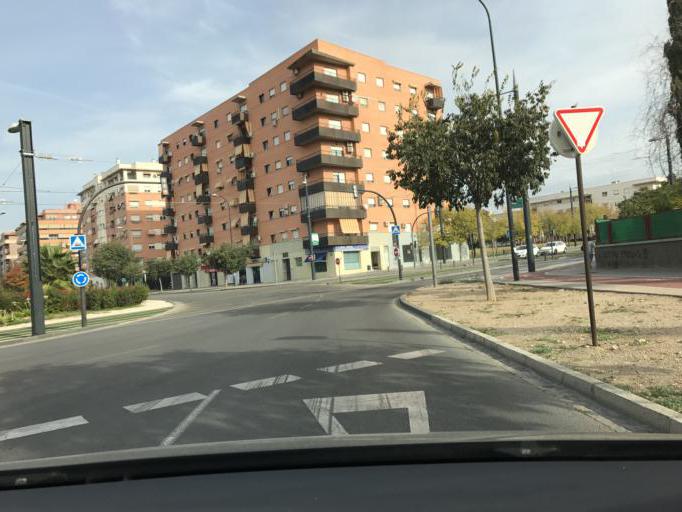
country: ES
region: Andalusia
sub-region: Provincia de Granada
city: Granada
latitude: 37.1973
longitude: -3.6148
